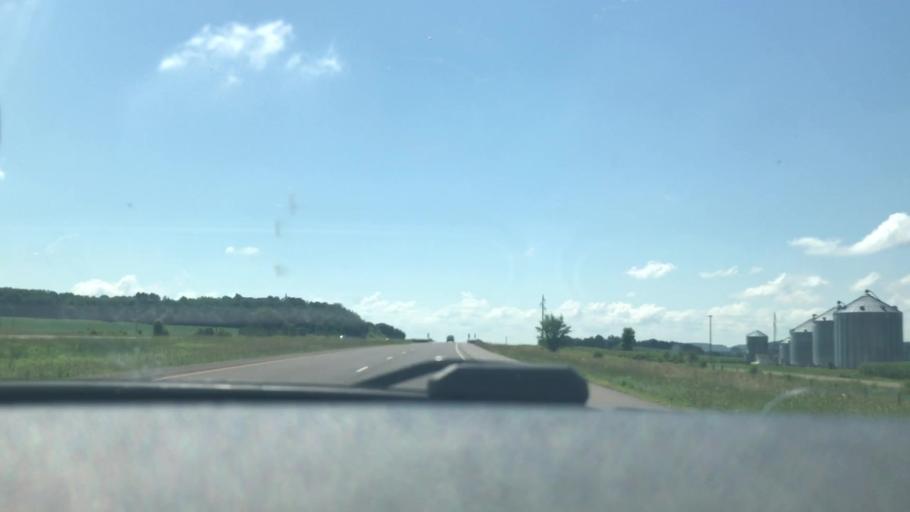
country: US
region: Wisconsin
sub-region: Chippewa County
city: Bloomer
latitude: 45.0339
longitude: -91.4527
